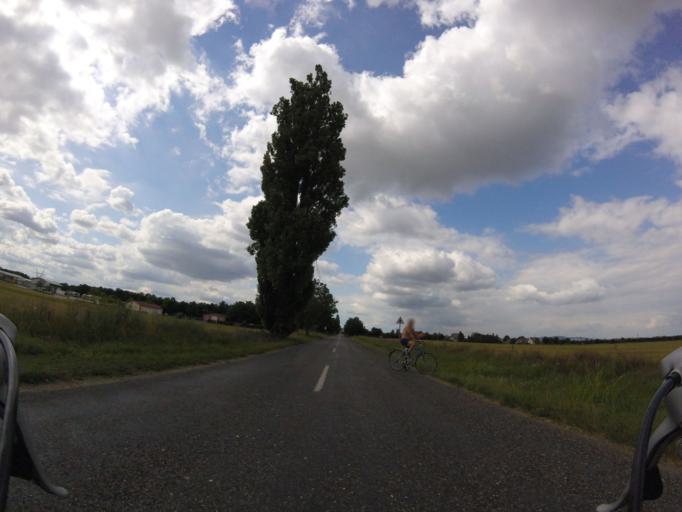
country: HU
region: Fejer
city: Seregelyes
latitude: 47.1666
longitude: 18.5728
